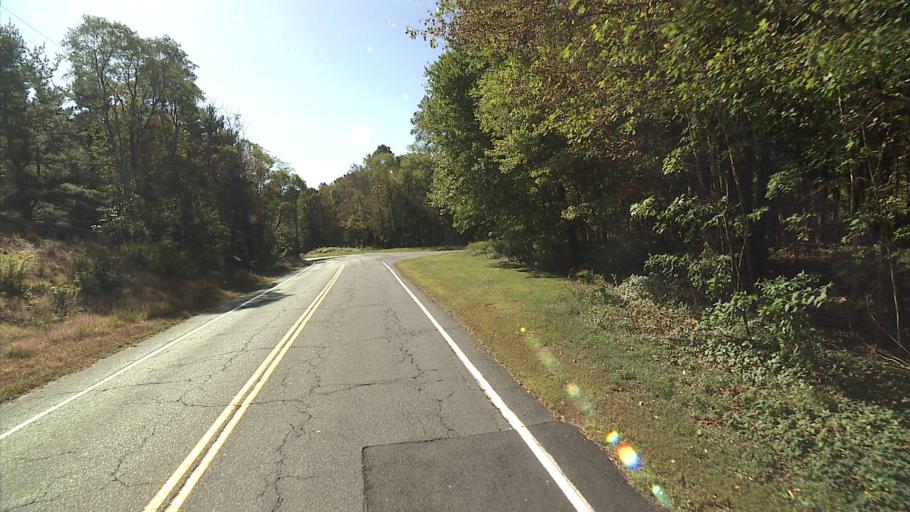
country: US
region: Connecticut
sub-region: Hartford County
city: Bristol
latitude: 41.7430
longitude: -72.9716
